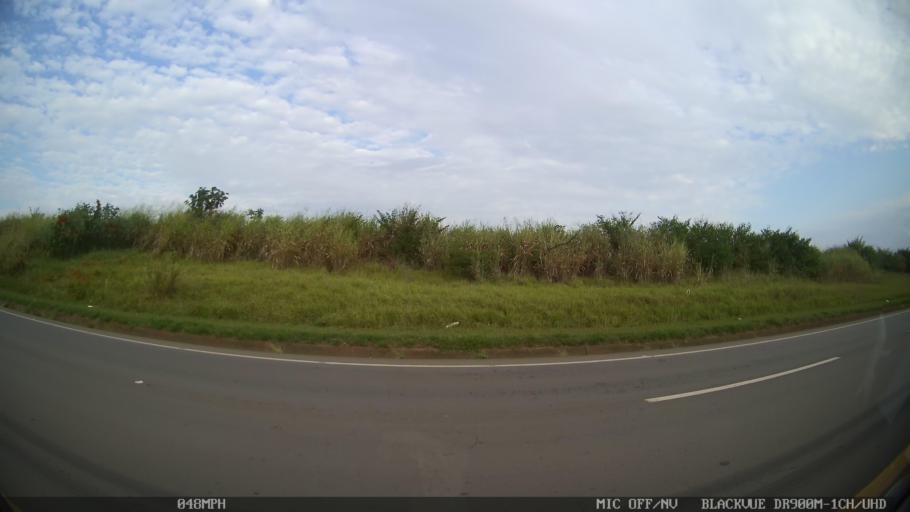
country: BR
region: Sao Paulo
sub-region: Cosmopolis
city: Cosmopolis
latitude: -22.6219
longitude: -47.2536
